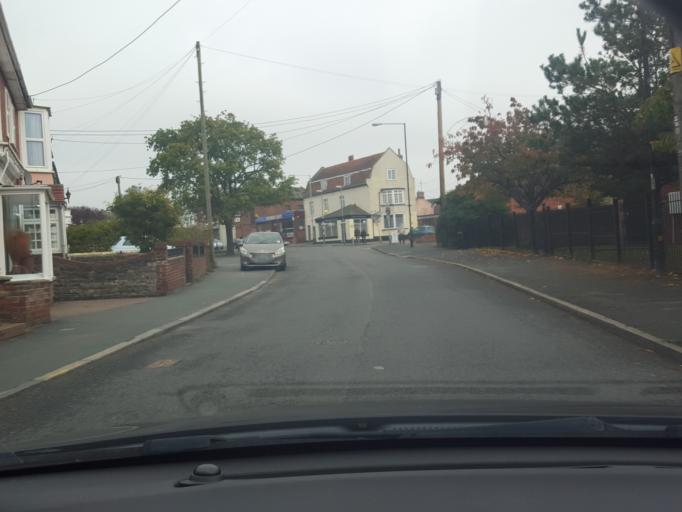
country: GB
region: England
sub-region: Essex
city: Brightlingsea
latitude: 51.8099
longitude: 1.0230
